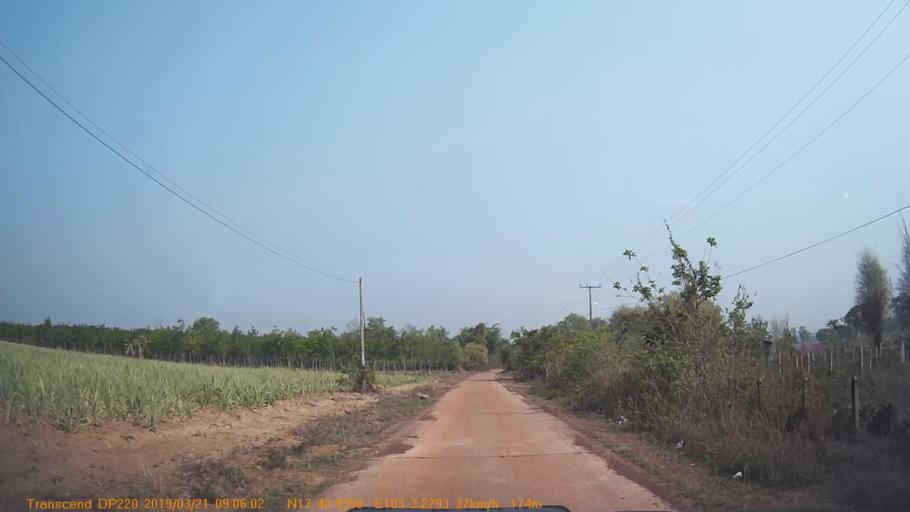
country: TH
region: Changwat Udon Thani
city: Phibun Rak
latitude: 17.6742
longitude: 103.0546
